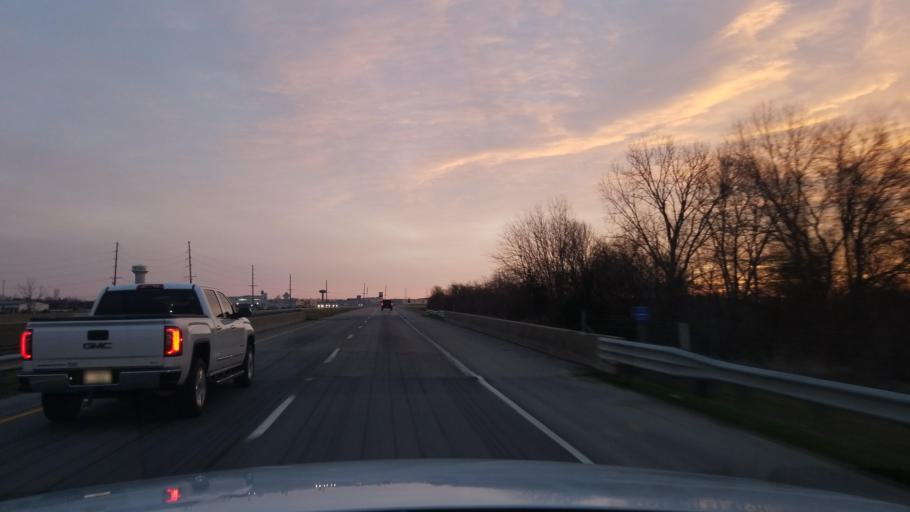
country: US
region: Indiana
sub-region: Posey County
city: Mount Vernon
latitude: 37.9413
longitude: -87.8598
